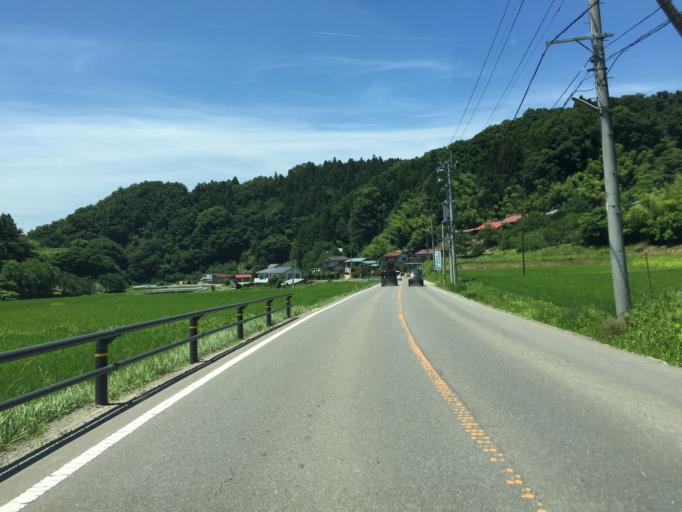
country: JP
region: Fukushima
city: Yanagawamachi-saiwaicho
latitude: 37.7603
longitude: 140.6409
